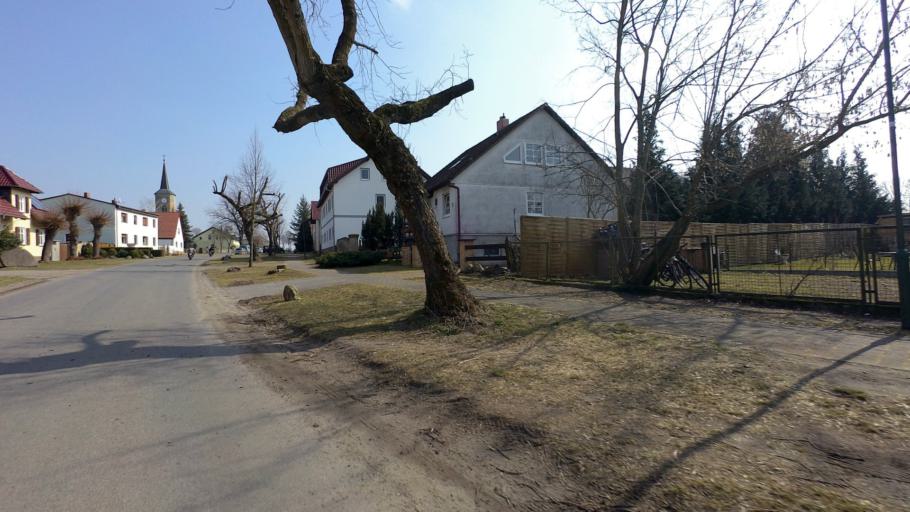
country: DE
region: Brandenburg
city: Gross Kreutz
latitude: 52.4165
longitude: 12.8005
